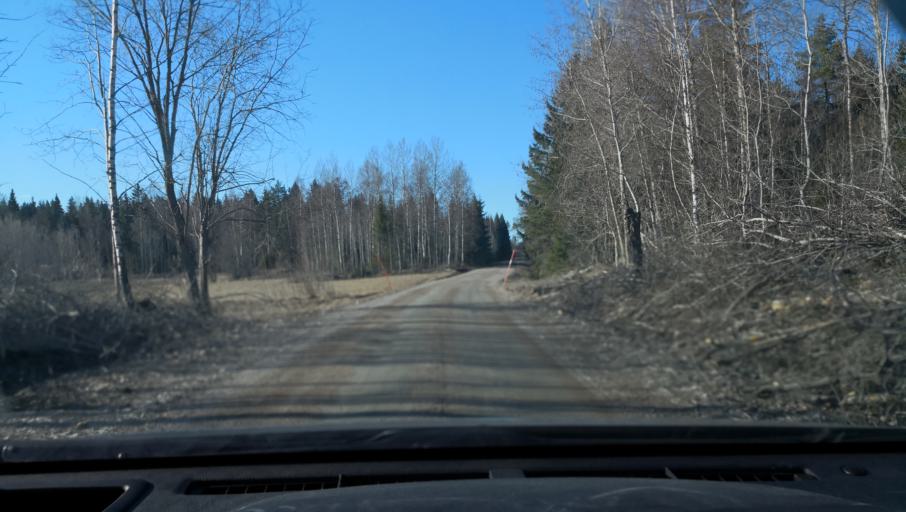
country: SE
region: Vaestmanland
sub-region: Sala Kommun
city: Sala
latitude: 60.1548
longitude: 16.6320
